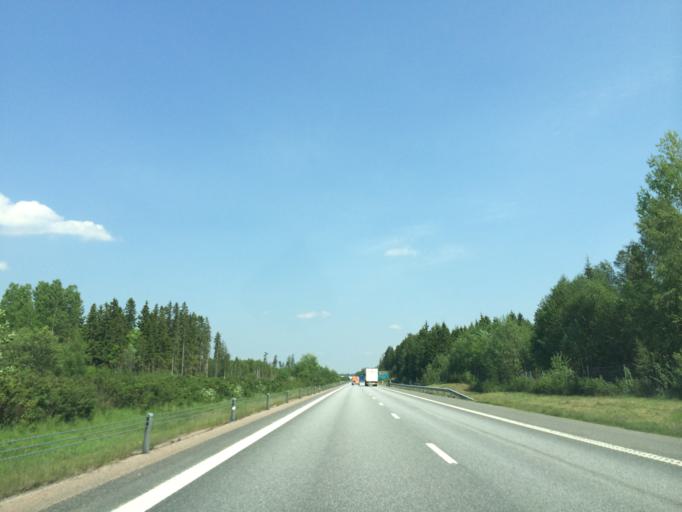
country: SE
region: Joenkoeping
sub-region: Varnamo Kommun
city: Varnamo
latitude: 57.1426
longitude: 14.0652
